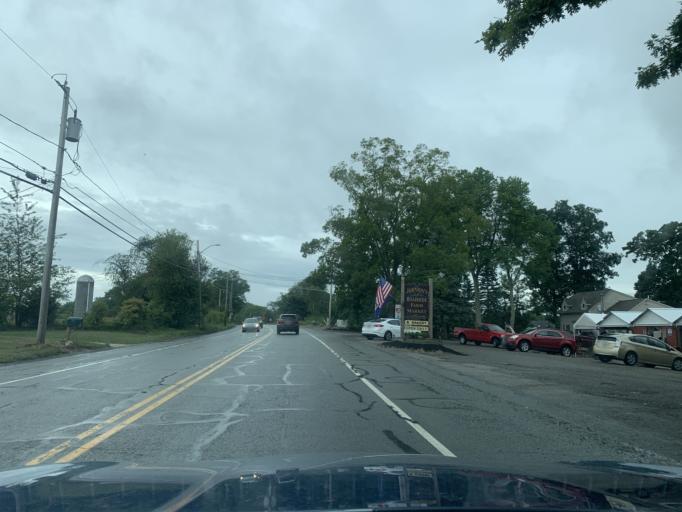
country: US
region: Rhode Island
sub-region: Bristol County
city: Warren
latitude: 41.7583
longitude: -71.2704
